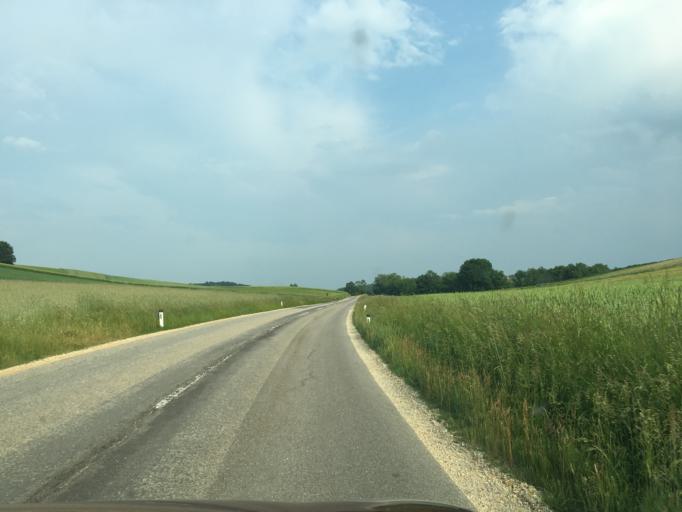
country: AT
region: Upper Austria
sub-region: Politischer Bezirk Ried im Innkreis
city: Waldzell
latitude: 48.1344
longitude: 13.4344
